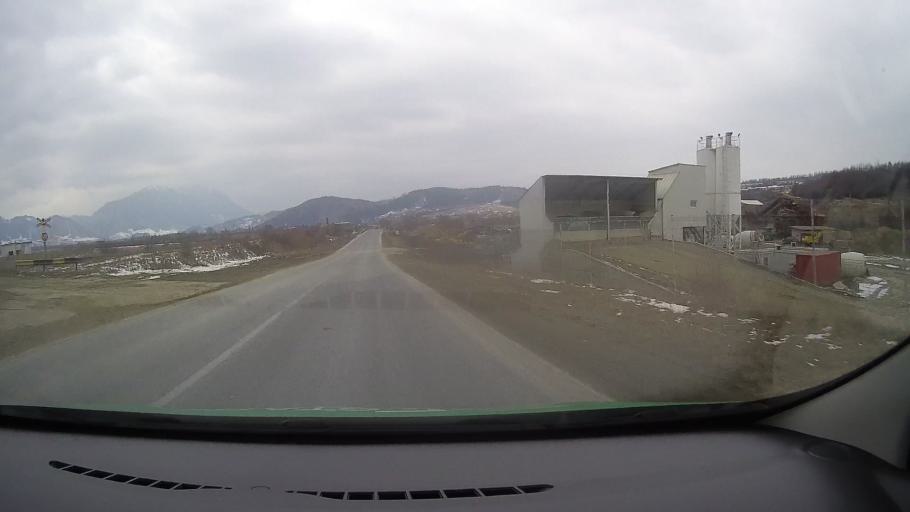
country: RO
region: Brasov
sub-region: Comuna Zarnesti
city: Tohanu Nou
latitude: 45.5770
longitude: 25.3947
